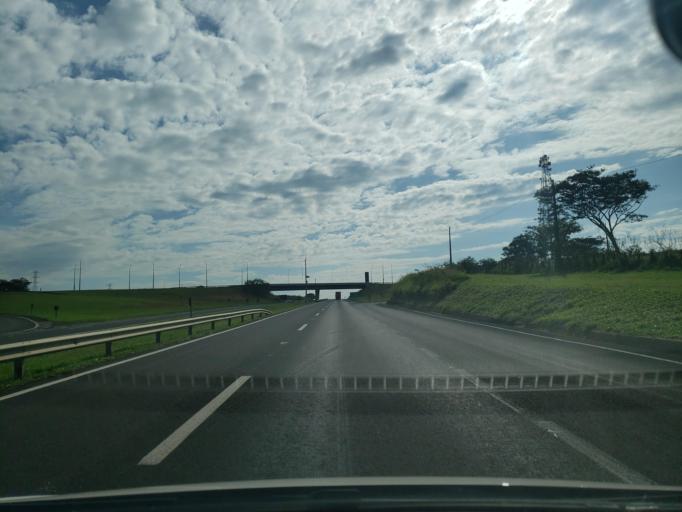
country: BR
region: Sao Paulo
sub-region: Lins
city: Lins
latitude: -21.6673
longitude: -49.7872
